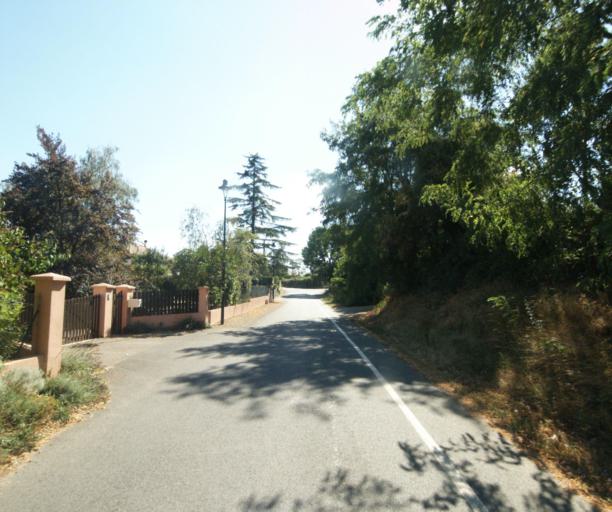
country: FR
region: Rhone-Alpes
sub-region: Departement du Rhone
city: La Tour-de-Salvagny
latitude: 45.8283
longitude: 4.7012
